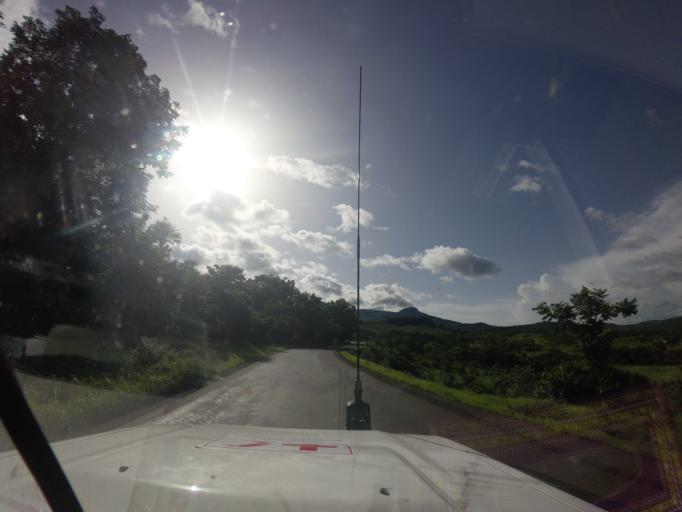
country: GN
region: Kindia
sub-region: Kindia
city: Kindia
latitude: 10.1777
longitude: -12.4714
